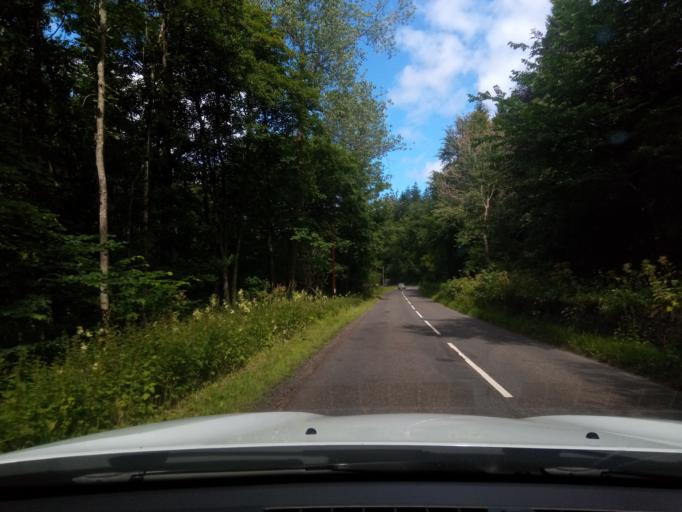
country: GB
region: Scotland
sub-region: The Scottish Borders
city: Selkirk
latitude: 55.5422
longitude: -2.8992
